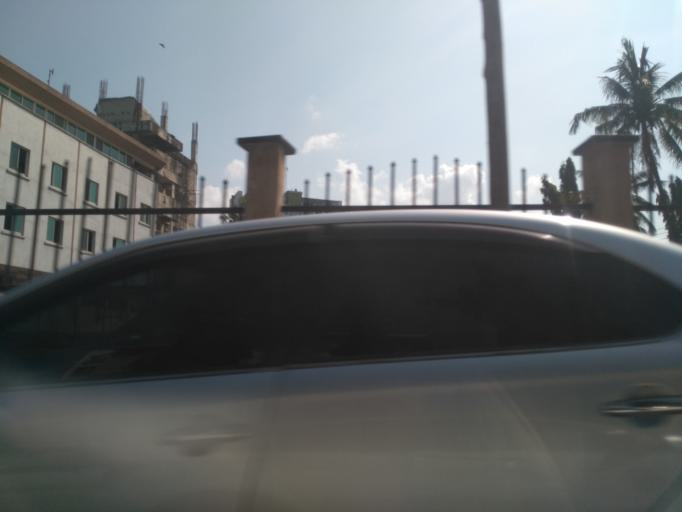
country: TZ
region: Dar es Salaam
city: Dar es Salaam
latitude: -6.8087
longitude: 39.2801
